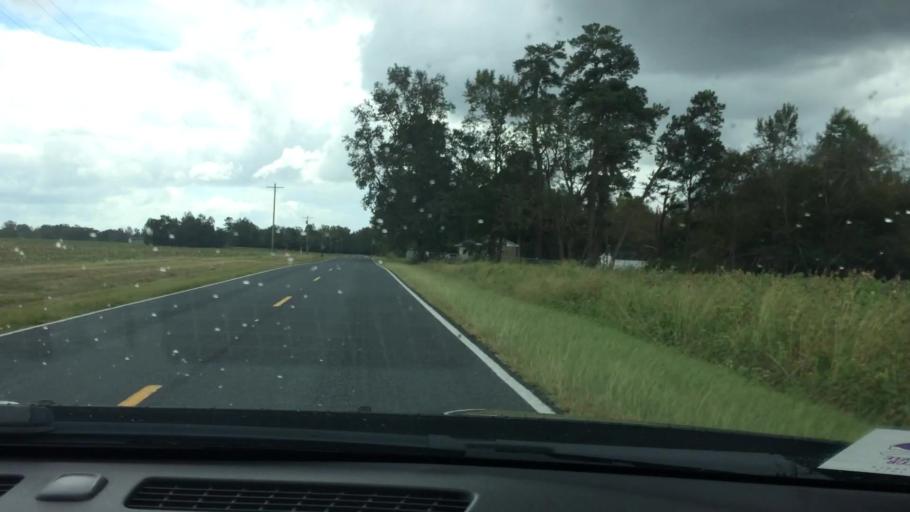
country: US
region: North Carolina
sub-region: Greene County
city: Maury
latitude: 35.5047
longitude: -77.5249
